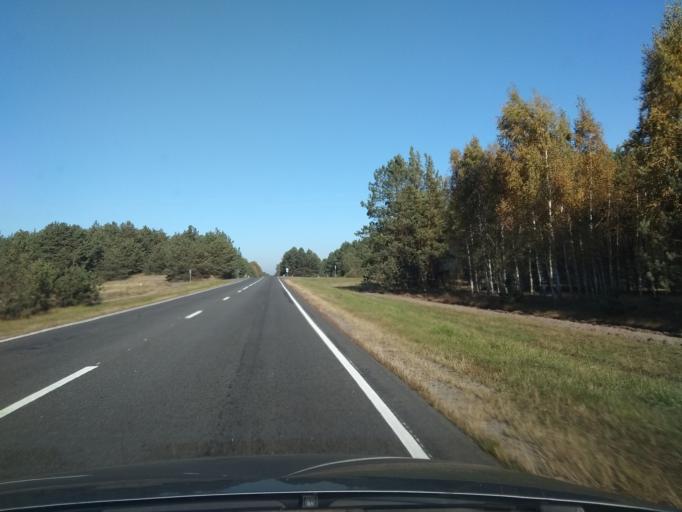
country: BY
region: Brest
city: Kobryn
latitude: 52.0714
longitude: 24.2833
